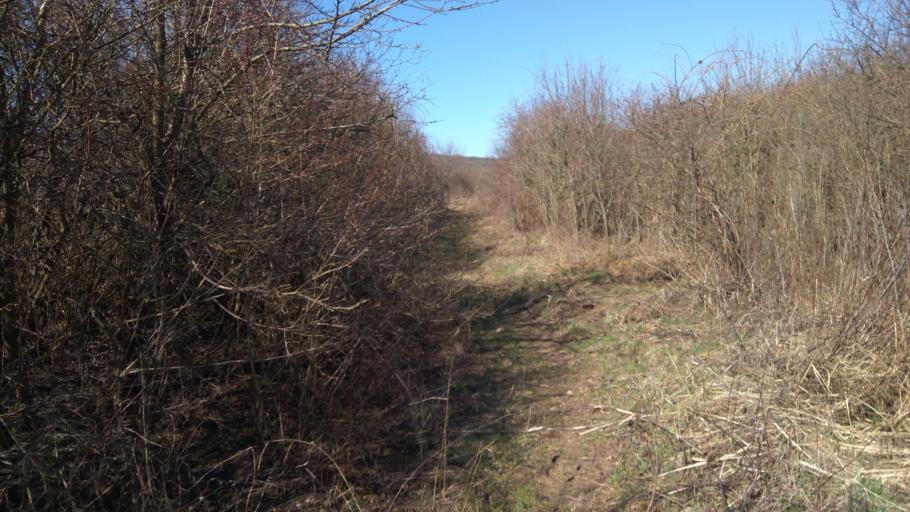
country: HU
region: Pest
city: Nagykovacsi
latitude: 47.6414
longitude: 18.9960
